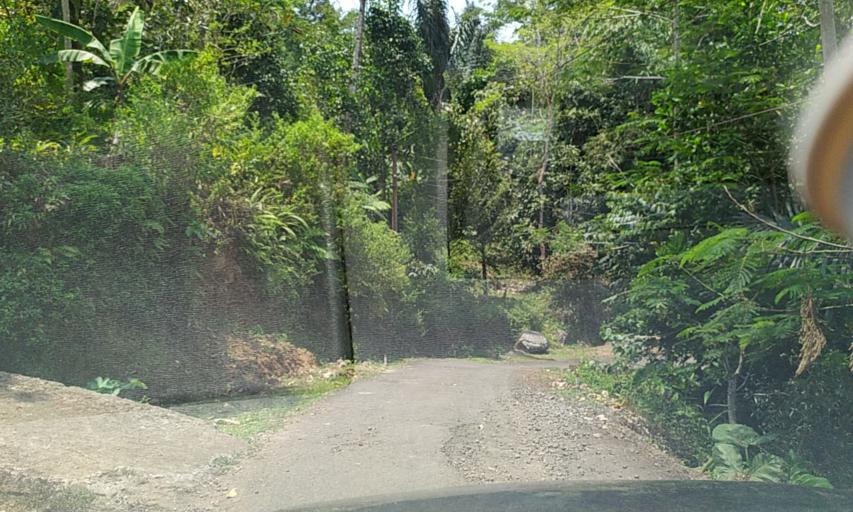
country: ID
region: Central Java
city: Kaduluhur
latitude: -7.1881
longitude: 108.6466
